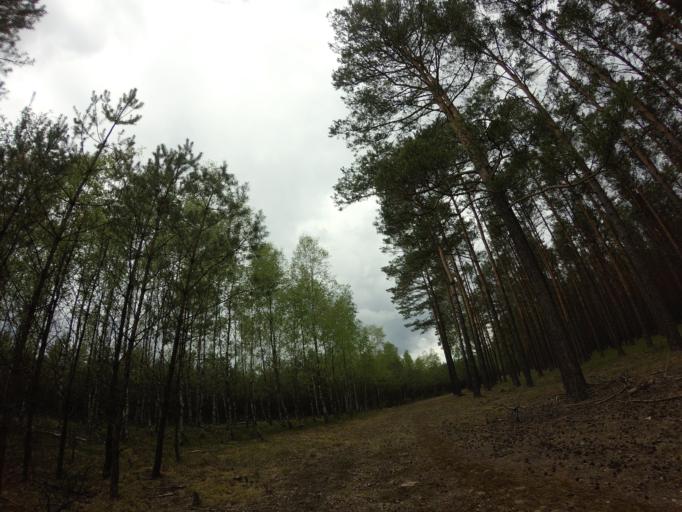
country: PL
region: West Pomeranian Voivodeship
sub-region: Powiat drawski
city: Kalisz Pomorski
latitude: 53.1889
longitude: 15.9833
